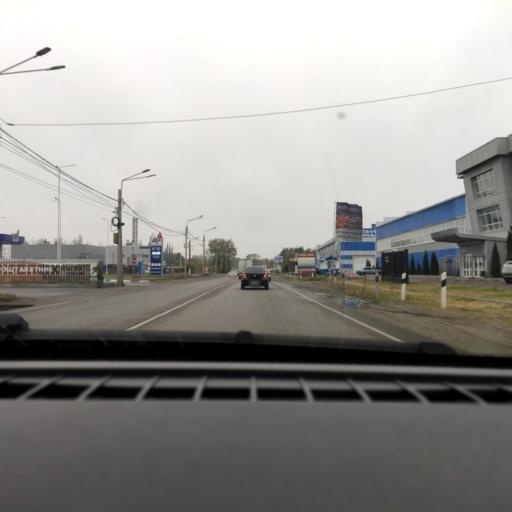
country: RU
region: Voronezj
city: Maslovka
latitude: 51.6376
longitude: 39.2920
